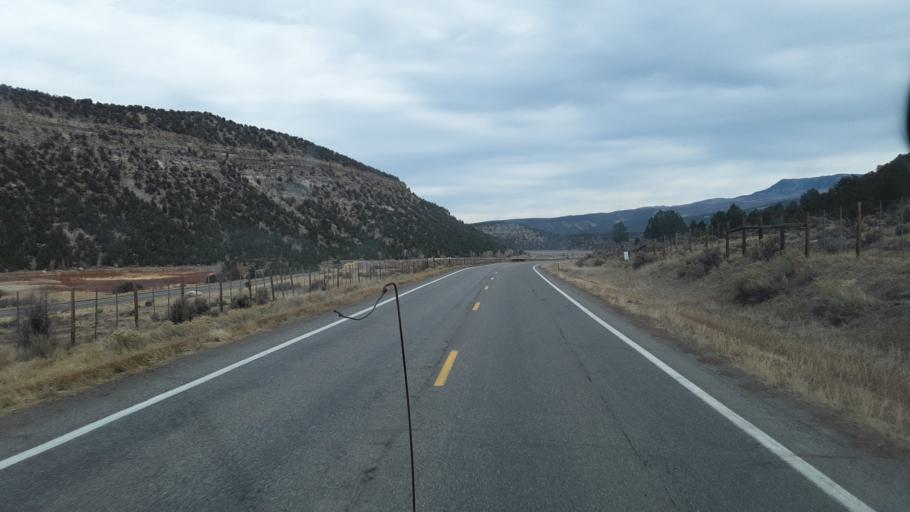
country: US
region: Colorado
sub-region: Ouray County
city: Ouray
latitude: 38.1906
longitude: -107.7454
